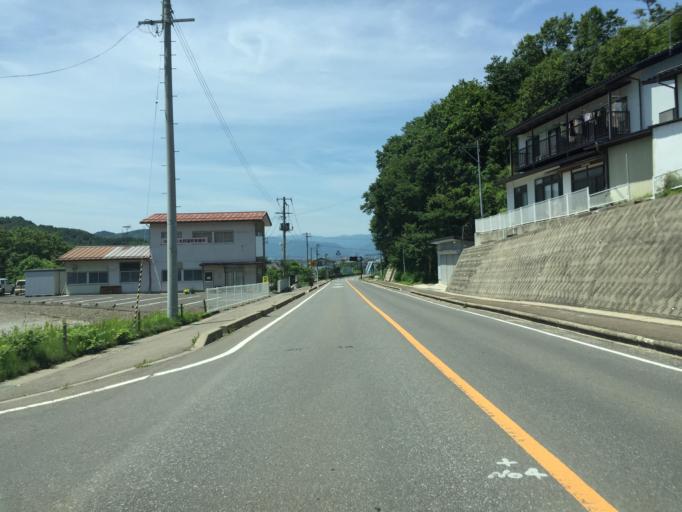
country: JP
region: Fukushima
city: Fukushima-shi
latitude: 37.7677
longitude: 140.5144
